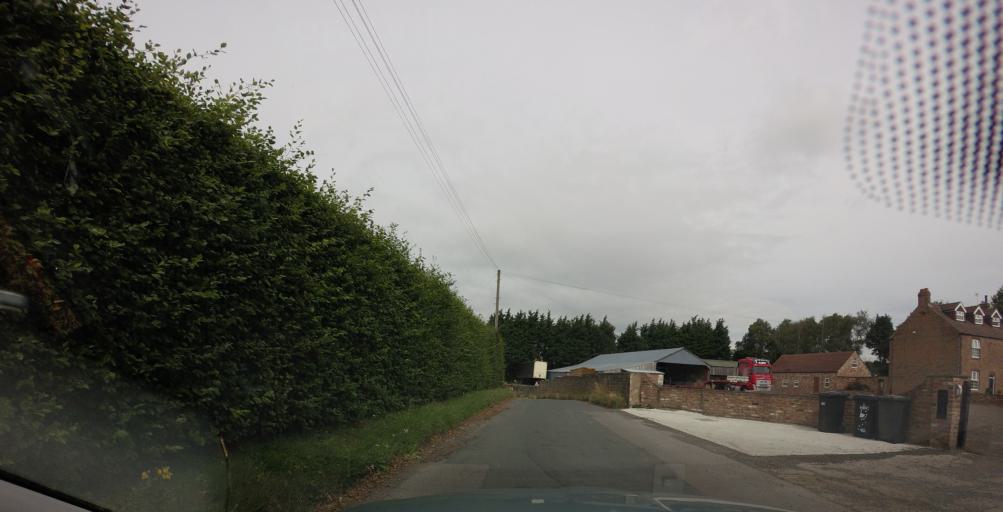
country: GB
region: England
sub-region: North Yorkshire
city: Ripon
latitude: 54.1288
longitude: -1.4844
